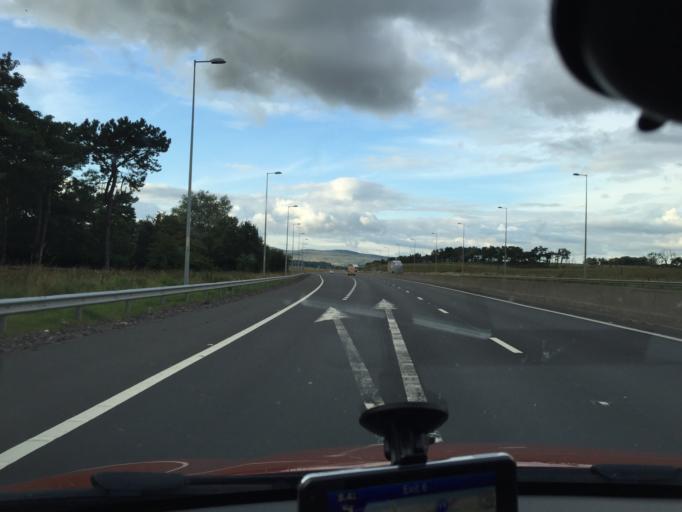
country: GB
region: Scotland
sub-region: North Lanarkshire
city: Glenboig
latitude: 55.9108
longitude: -4.0657
